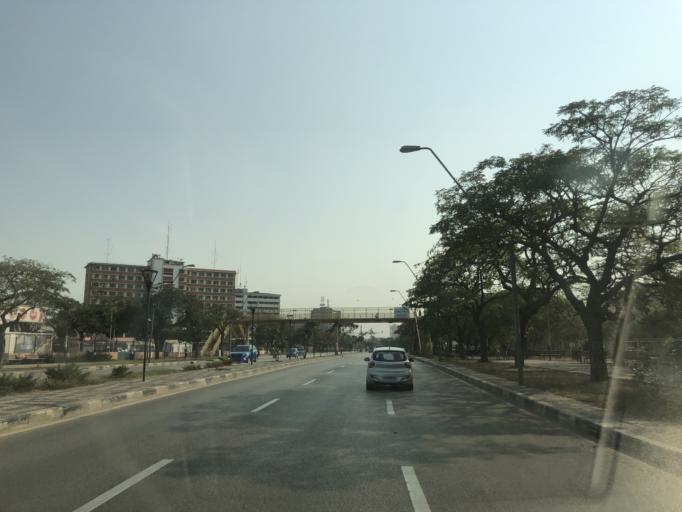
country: AO
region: Luanda
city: Luanda
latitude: -8.8317
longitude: 13.2406
